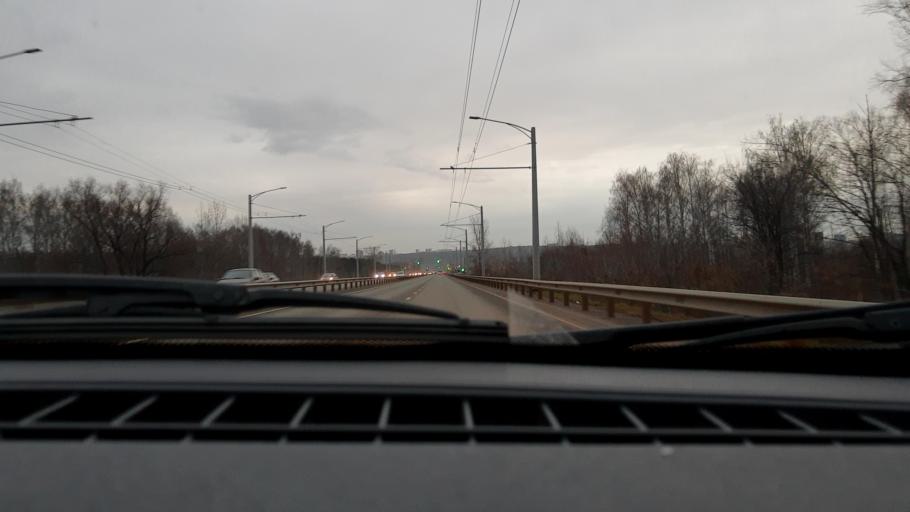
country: RU
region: Bashkortostan
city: Ufa
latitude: 54.7677
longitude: 55.9301
